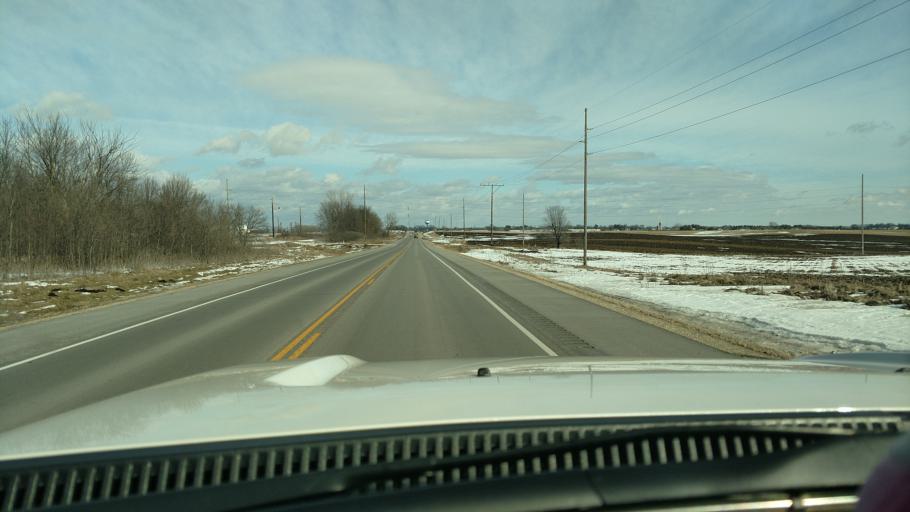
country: US
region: Minnesota
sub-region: Wabasha County
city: Plainview
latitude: 44.1534
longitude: -92.2017
